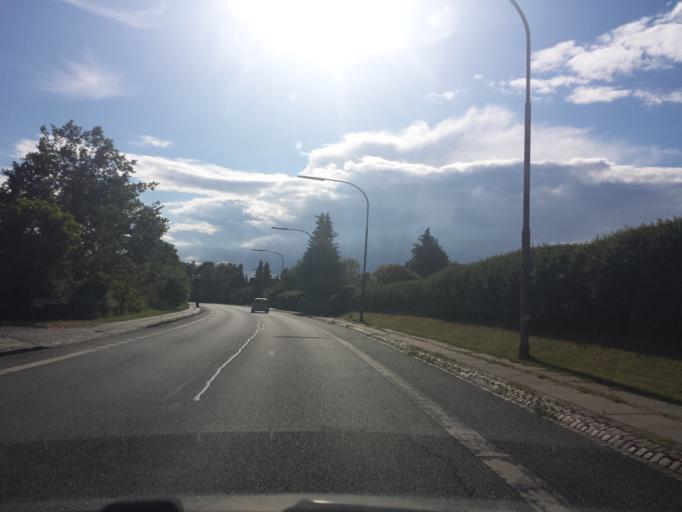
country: DK
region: Capital Region
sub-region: Ballerup Kommune
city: Malov
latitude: 55.7549
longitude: 12.3294
